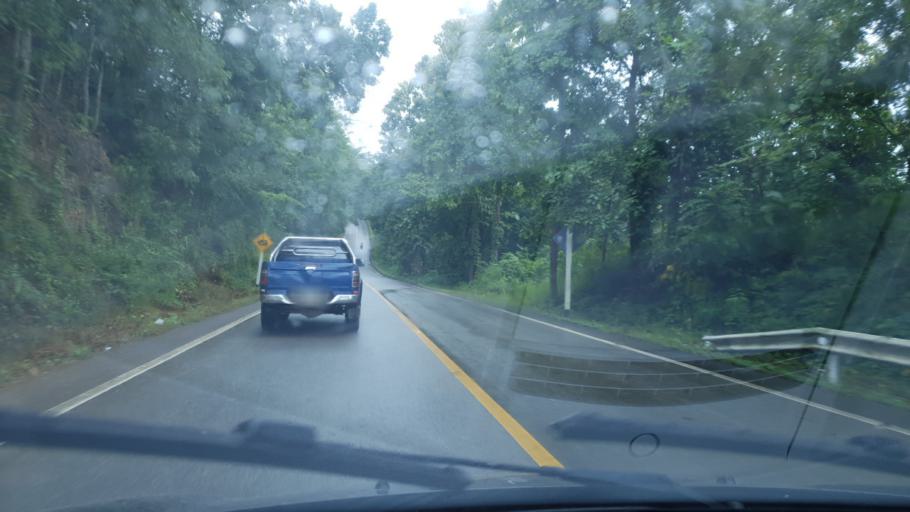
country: TH
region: Mae Hong Son
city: Mae La Noi
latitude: 18.2916
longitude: 97.9189
